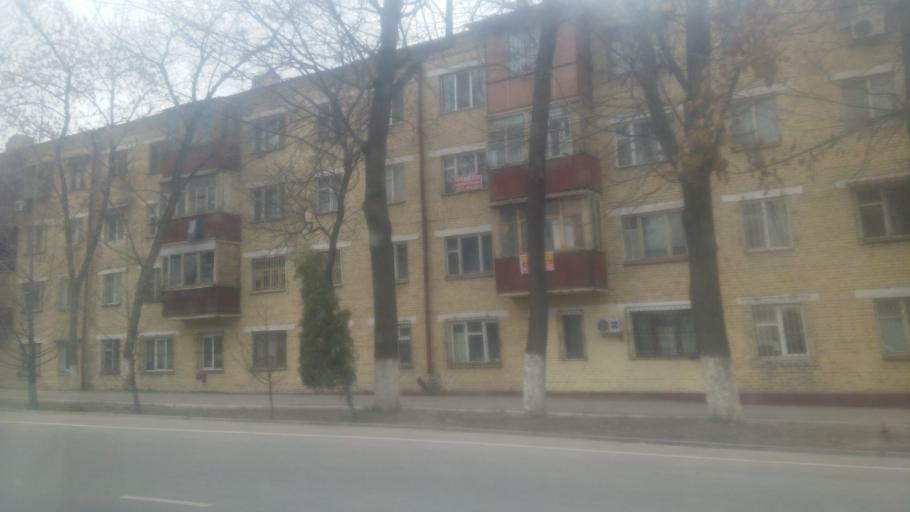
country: UZ
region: Toshkent
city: Salor
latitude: 41.3378
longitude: 69.3317
